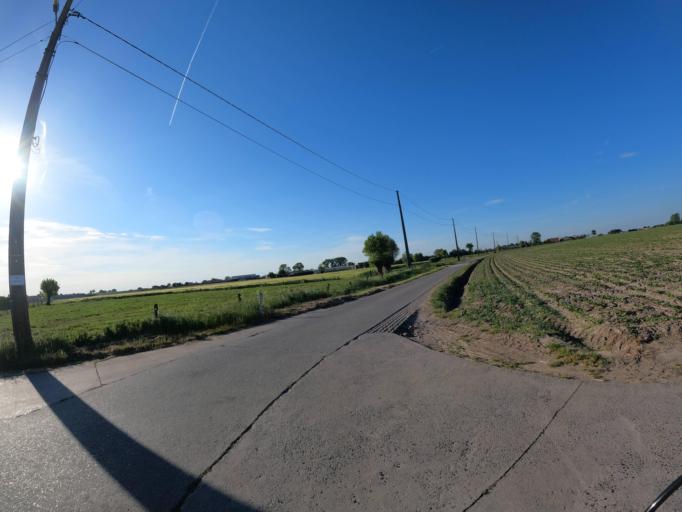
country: BE
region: Flanders
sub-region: Provincie West-Vlaanderen
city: Dentergem
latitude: 50.9974
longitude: 3.4501
